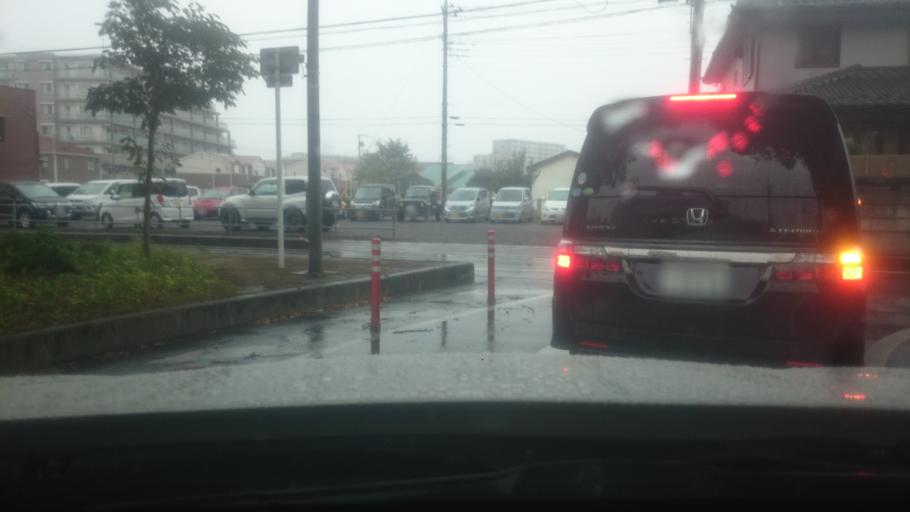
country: JP
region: Saitama
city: Kamifukuoka
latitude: 35.8717
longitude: 139.5037
